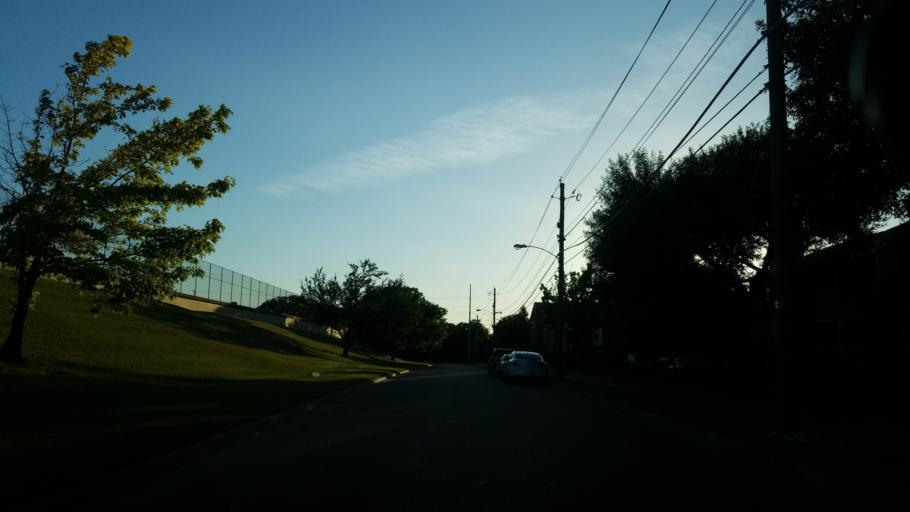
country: US
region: Texas
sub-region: Dallas County
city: Balch Springs
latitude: 32.7885
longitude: -96.6982
